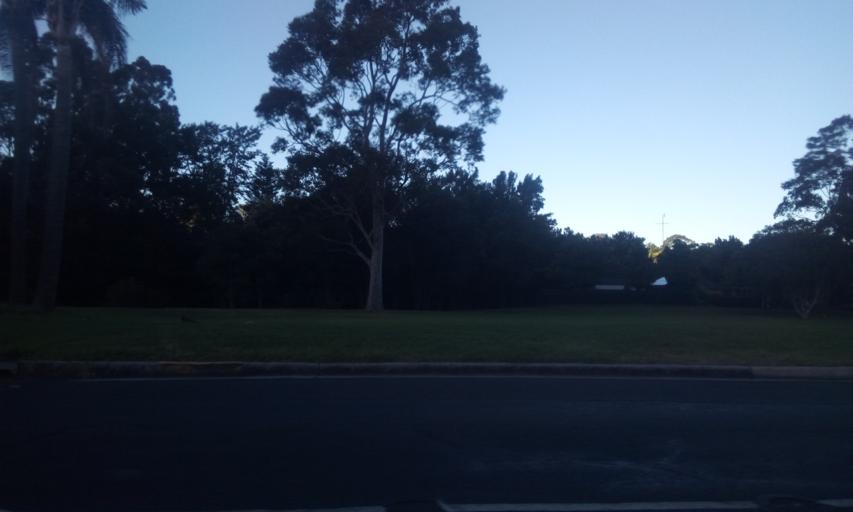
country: AU
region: New South Wales
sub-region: Wollongong
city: Mount Keira
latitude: -34.4184
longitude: 150.8554
